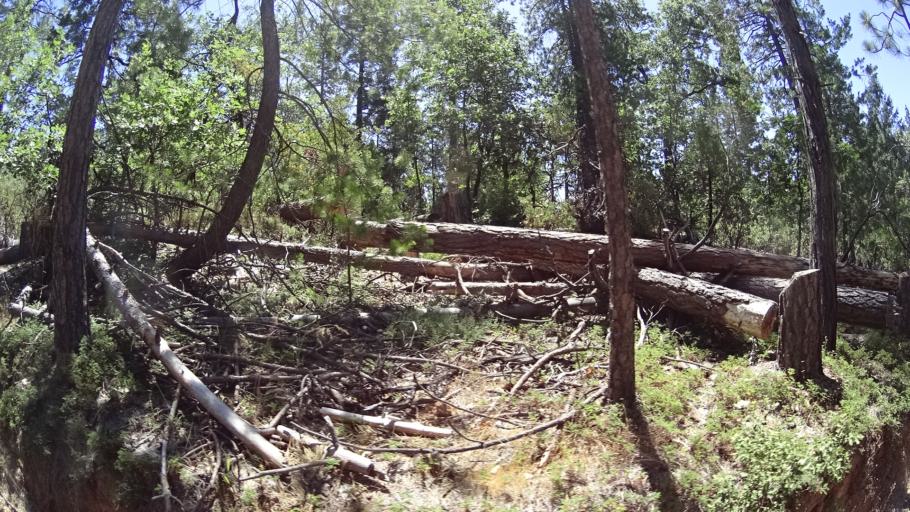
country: US
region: California
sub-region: Amador County
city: Pioneer
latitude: 38.4130
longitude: -120.5068
